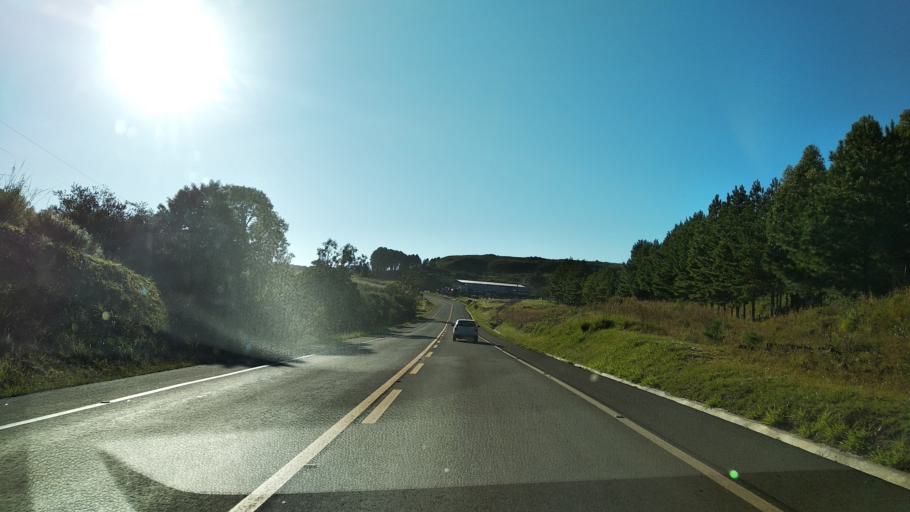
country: BR
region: Santa Catarina
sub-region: Lages
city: Lages
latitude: -27.7882
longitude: -50.4326
